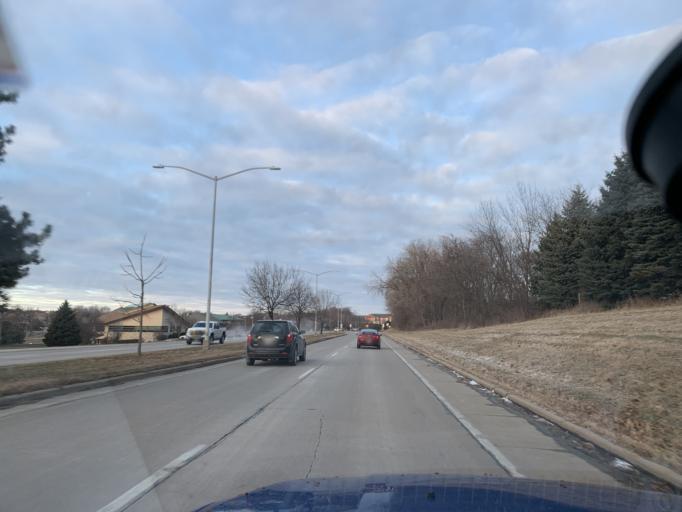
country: US
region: Wisconsin
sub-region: Dane County
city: Fitchburg
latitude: 43.0118
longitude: -89.4281
